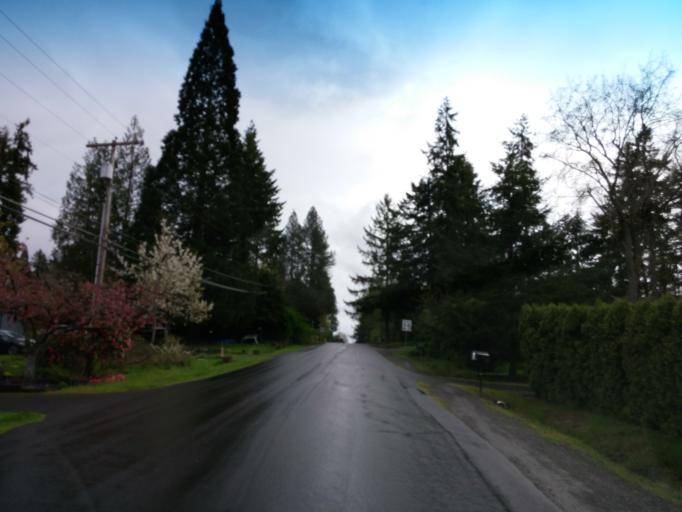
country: US
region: Oregon
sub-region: Washington County
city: Cedar Mill
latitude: 45.5213
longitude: -122.8252
